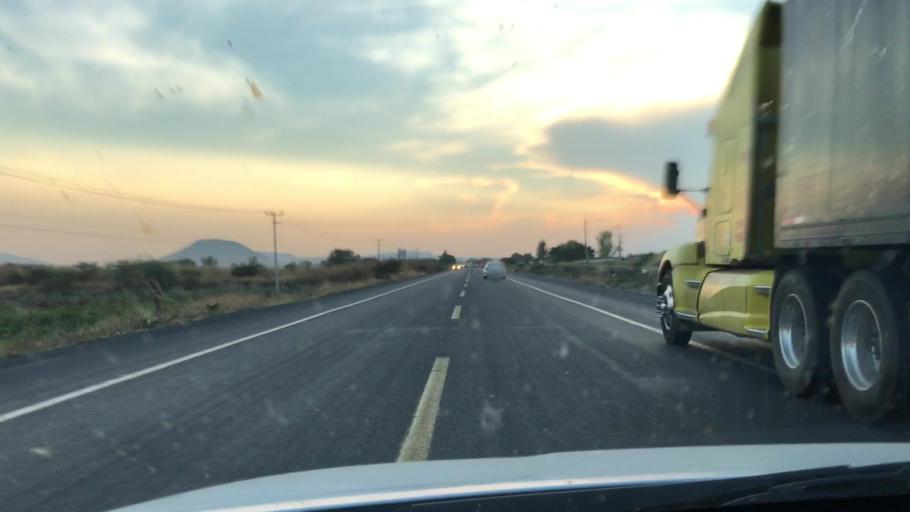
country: MX
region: Michoacan
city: Tanhuato de Guerrero
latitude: 20.3131
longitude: -102.3089
